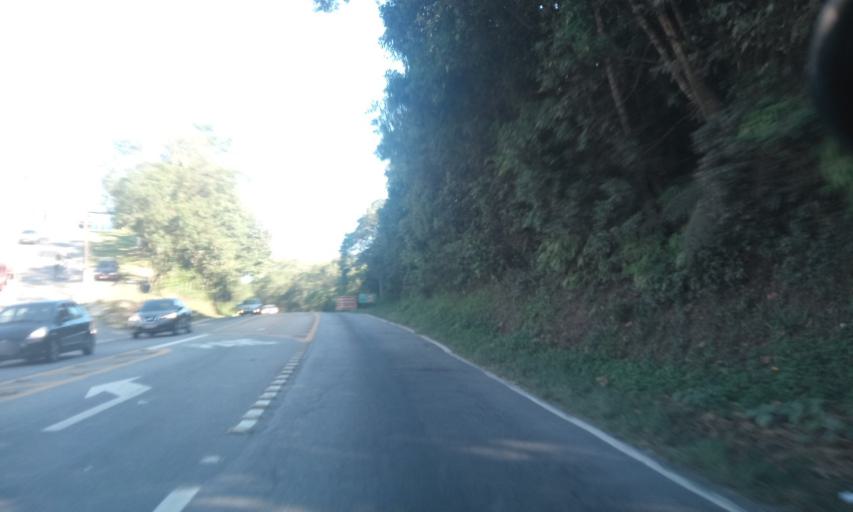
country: BR
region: Sao Paulo
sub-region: Sao Bernardo Do Campo
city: Sao Bernardo do Campo
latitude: -23.7876
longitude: -46.5069
